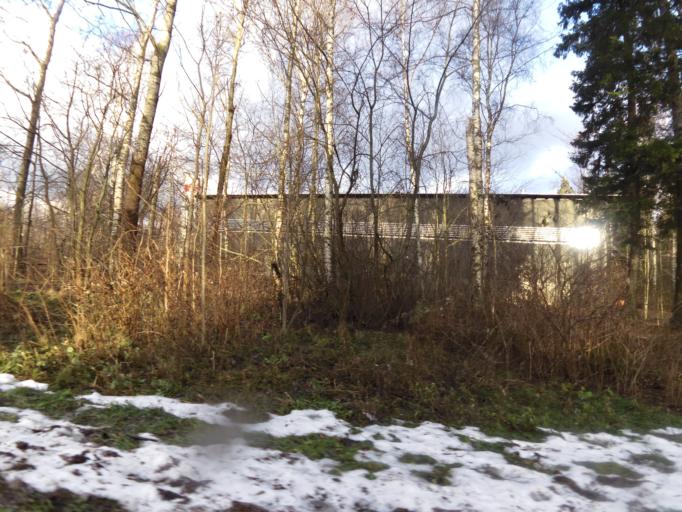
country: FI
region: Uusimaa
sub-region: Helsinki
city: Kilo
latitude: 60.2016
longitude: 24.7758
